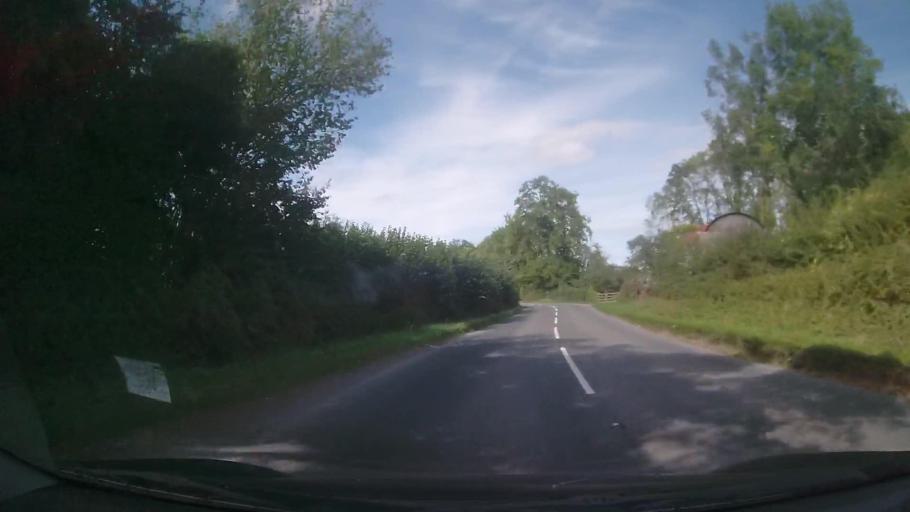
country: GB
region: England
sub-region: Herefordshire
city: Kington
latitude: 52.1633
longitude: -3.0175
